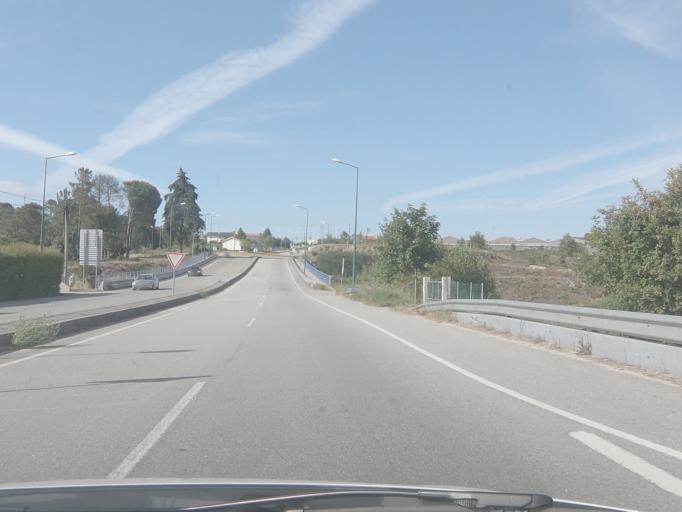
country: PT
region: Viseu
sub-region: Viseu
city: Viseu
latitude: 40.6232
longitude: -7.9442
